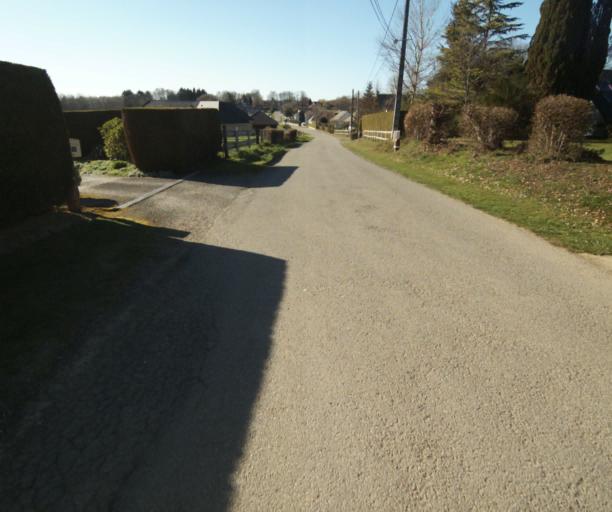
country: FR
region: Limousin
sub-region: Departement de la Correze
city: Seilhac
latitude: 45.3863
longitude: 1.7148
